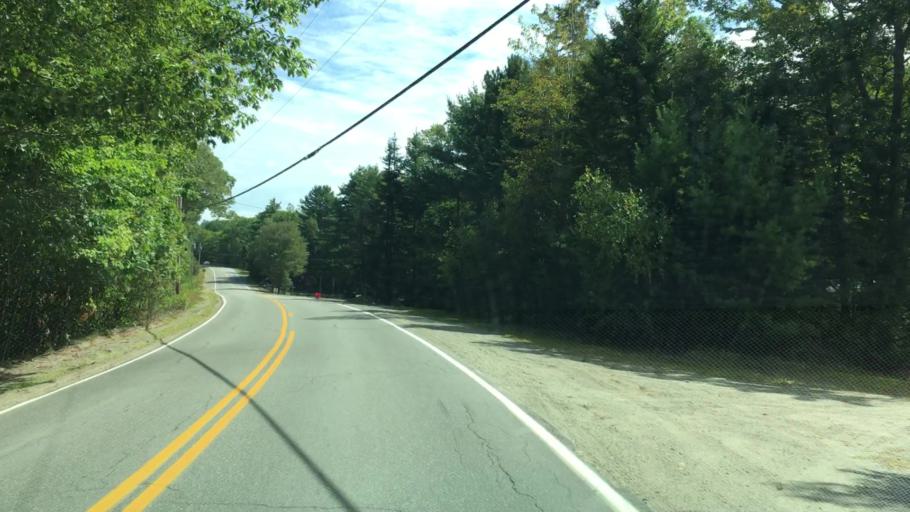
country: US
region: Maine
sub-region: Penobscot County
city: Holden
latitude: 44.7944
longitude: -68.5281
